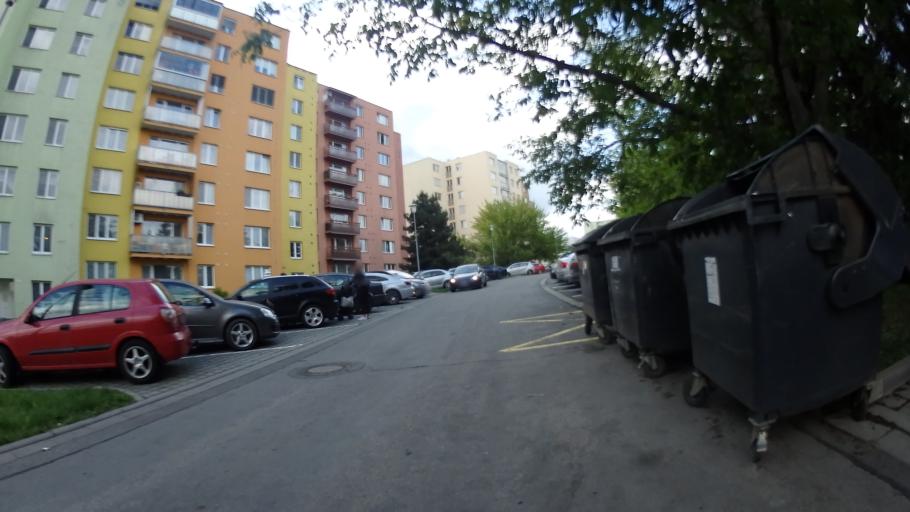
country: CZ
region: South Moravian
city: Moravany
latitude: 49.1656
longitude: 16.5722
